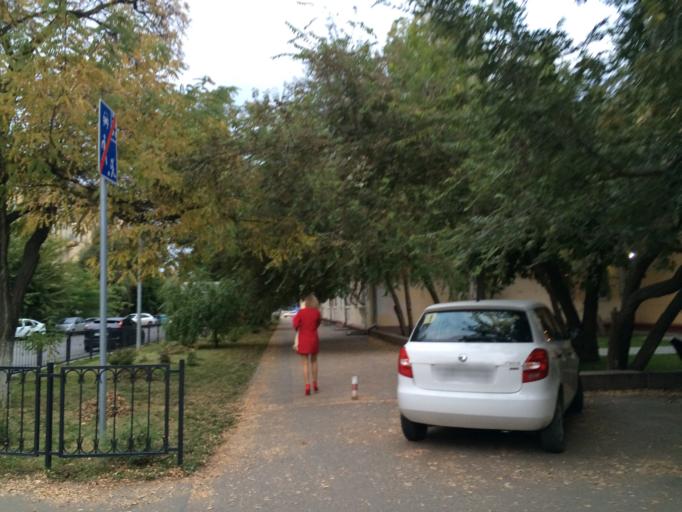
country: RU
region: Volgograd
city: Volgograd
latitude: 48.7131
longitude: 44.5223
